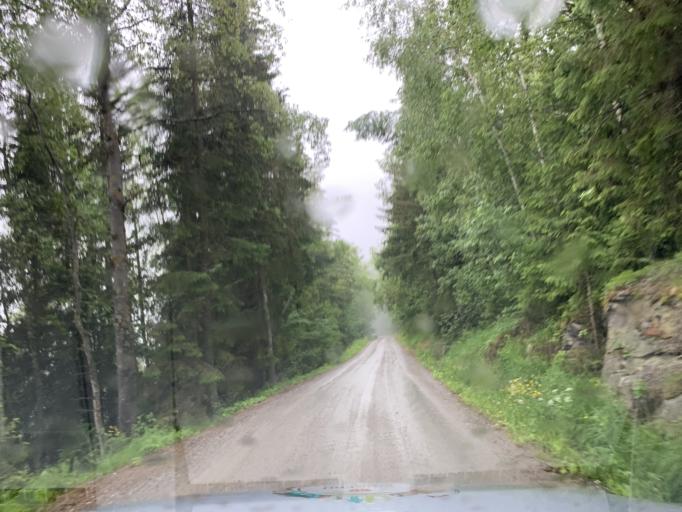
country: NO
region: Oppland
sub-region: Oyer
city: Tretten
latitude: 61.3904
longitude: 10.2617
